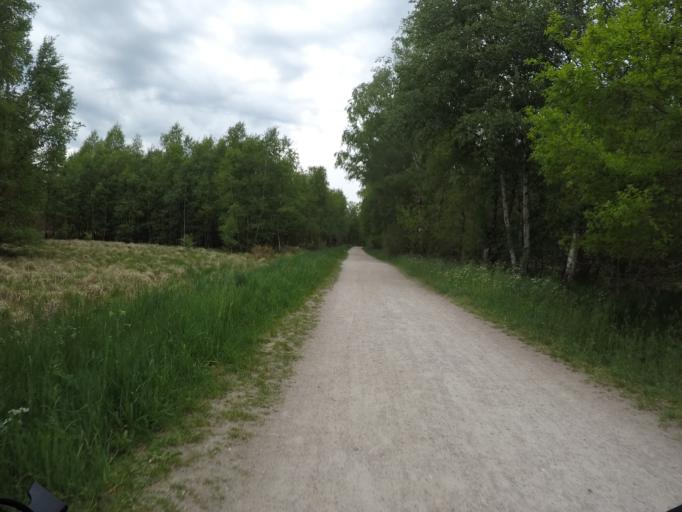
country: DE
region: Schleswig-Holstein
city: Henstedt-Ulzburg
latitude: 53.7559
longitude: 10.0164
